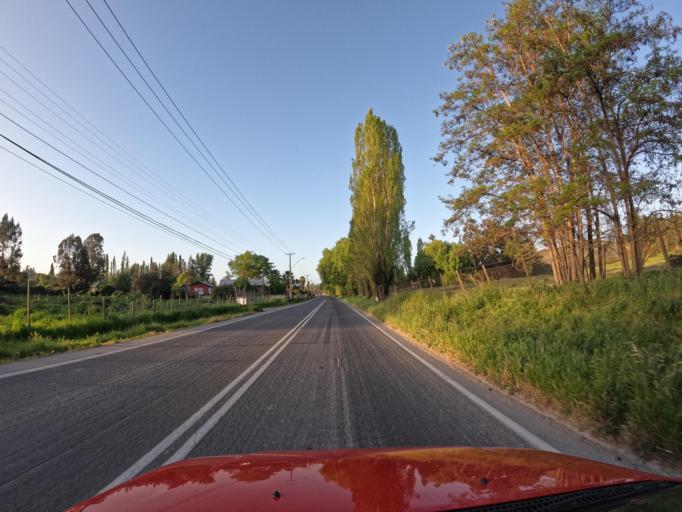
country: CL
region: O'Higgins
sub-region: Provincia de Cachapoal
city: San Vicente
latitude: -34.1882
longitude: -71.4029
